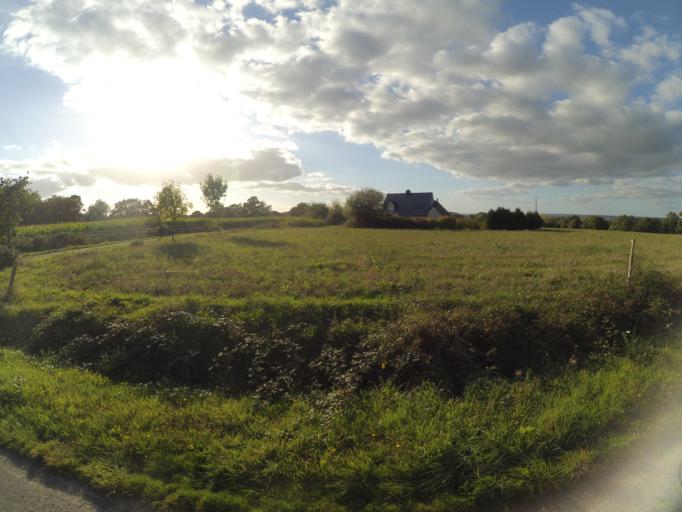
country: FR
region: Brittany
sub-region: Departement du Morbihan
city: Peillac
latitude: 47.7168
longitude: -2.1931
